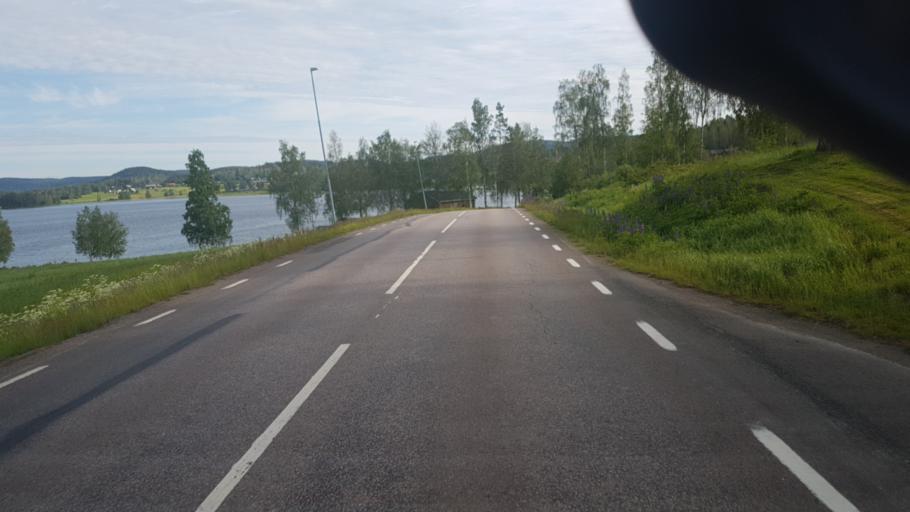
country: SE
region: Vaermland
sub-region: Arvika Kommun
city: Arvika
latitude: 59.7793
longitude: 12.6167
